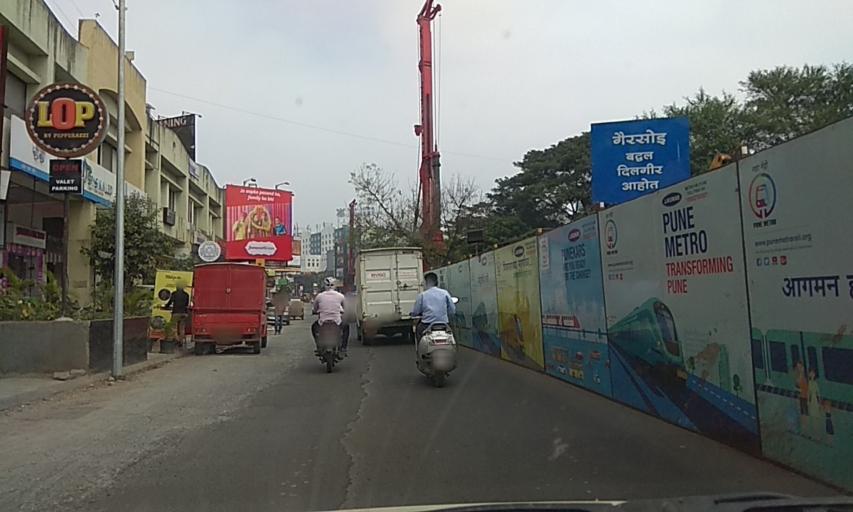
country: IN
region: Maharashtra
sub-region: Pune Division
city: Shivaji Nagar
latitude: 18.5436
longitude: 73.9052
